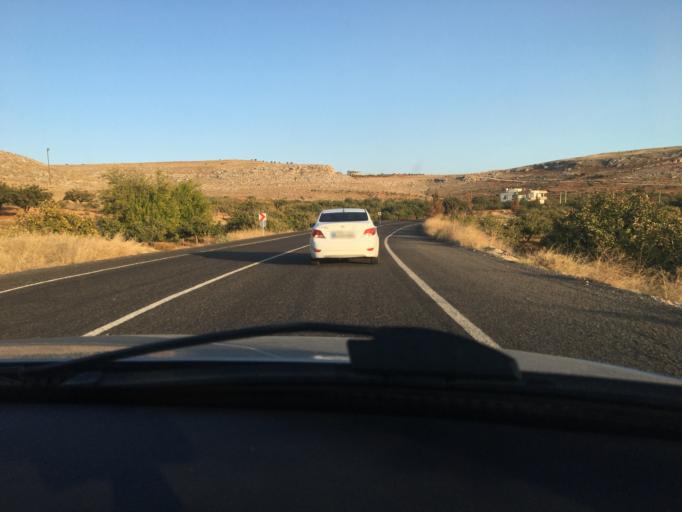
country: TR
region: Sanliurfa
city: Halfeti
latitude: 37.2158
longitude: 37.9601
